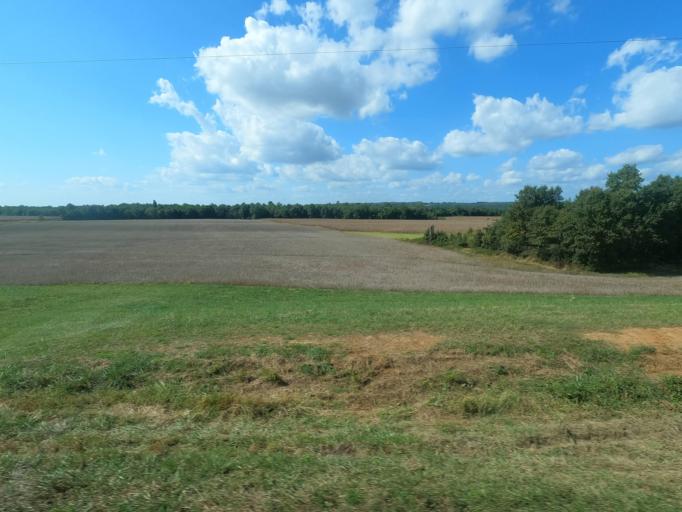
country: US
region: Illinois
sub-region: Massac County
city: Metropolis
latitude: 37.2734
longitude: -88.7565
